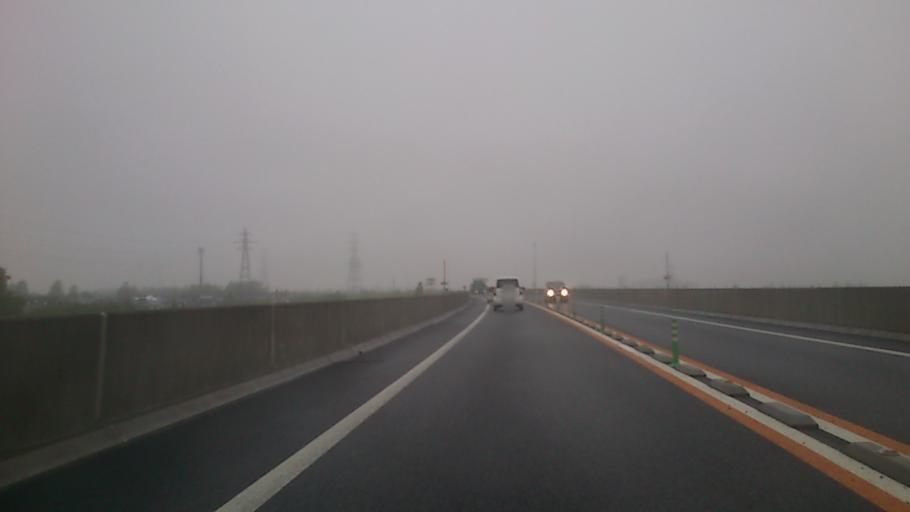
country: JP
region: Hokkaido
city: Kushiro
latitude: 43.0170
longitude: 144.4221
